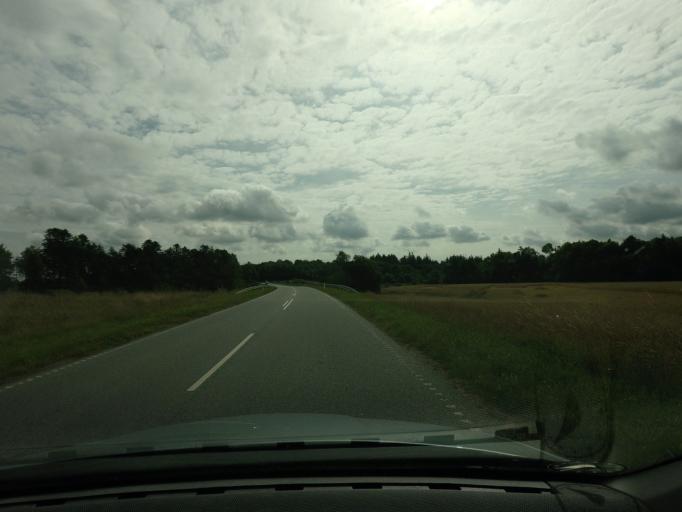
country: DK
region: North Denmark
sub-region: Bronderslev Kommune
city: Dronninglund
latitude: 57.2802
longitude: 10.2692
